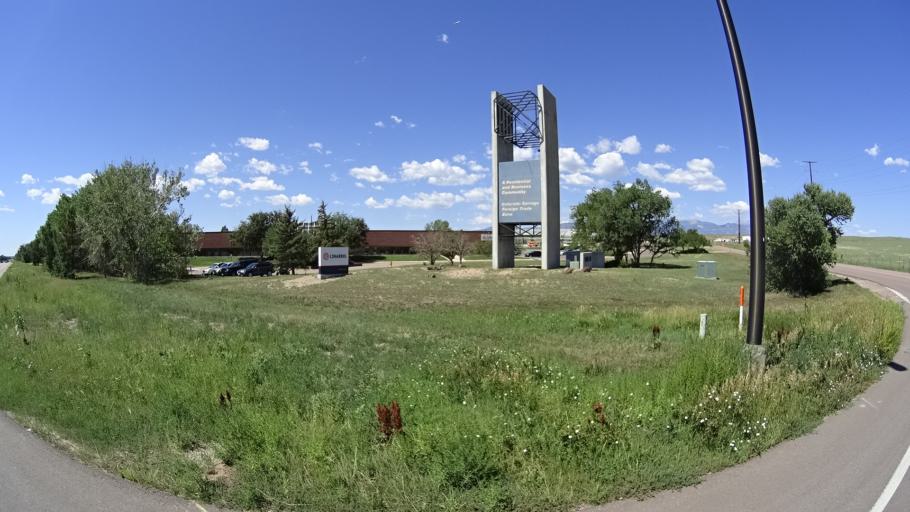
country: US
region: Colorado
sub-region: El Paso County
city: Security-Widefield
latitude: 38.7809
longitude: -104.6599
